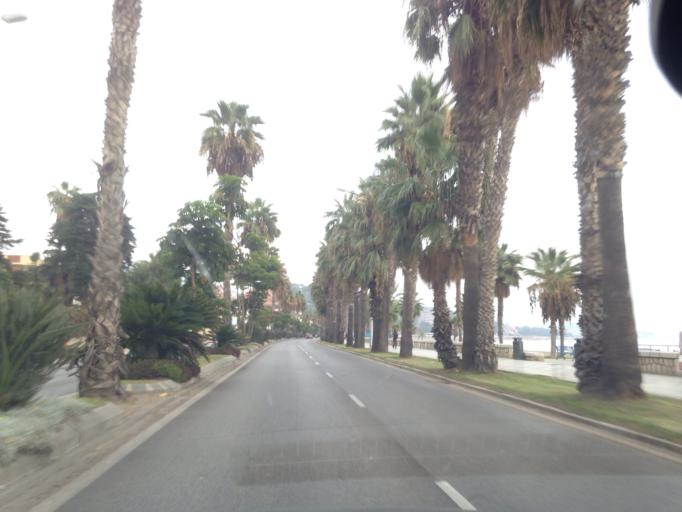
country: ES
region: Andalusia
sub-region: Provincia de Malaga
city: Malaga
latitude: 36.7209
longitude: -4.4019
